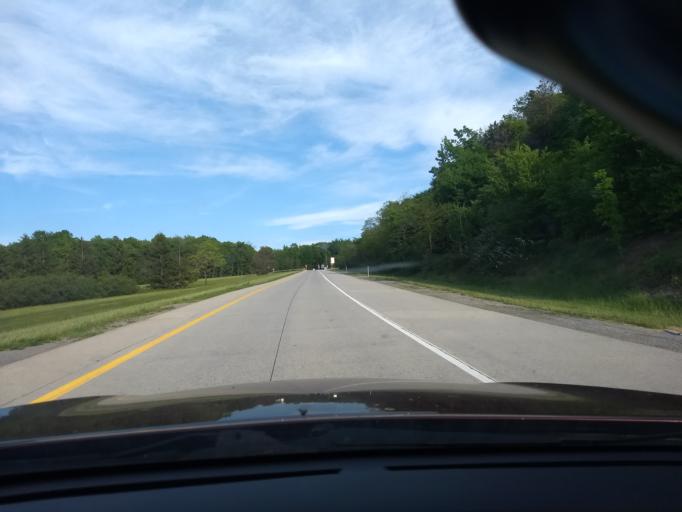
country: US
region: Pennsylvania
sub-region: Cambria County
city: Gallitzin
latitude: 40.4663
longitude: -78.5485
